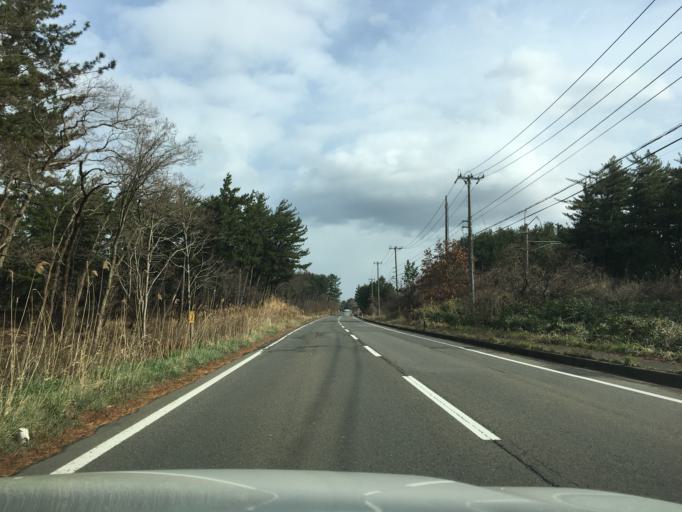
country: JP
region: Yamagata
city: Yuza
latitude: 39.2299
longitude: 139.9070
